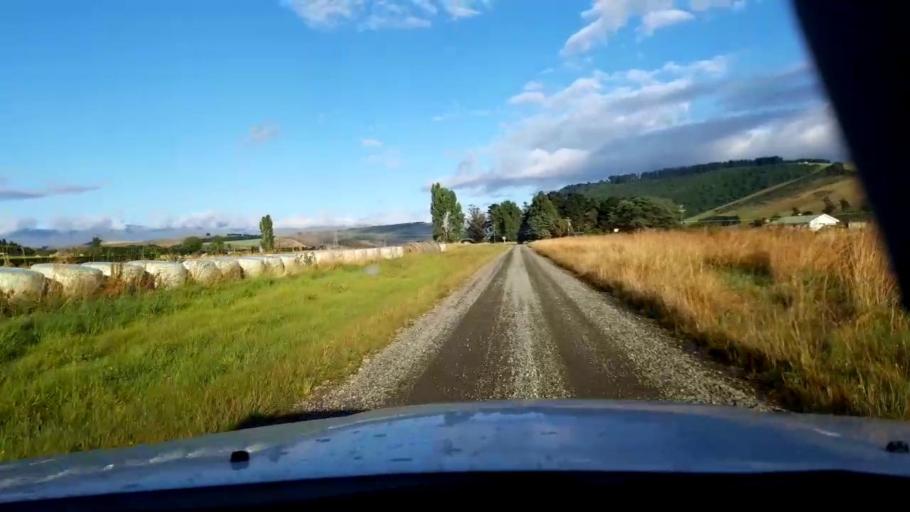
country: NZ
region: Canterbury
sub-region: Timaru District
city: Timaru
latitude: -44.4239
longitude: 171.1078
